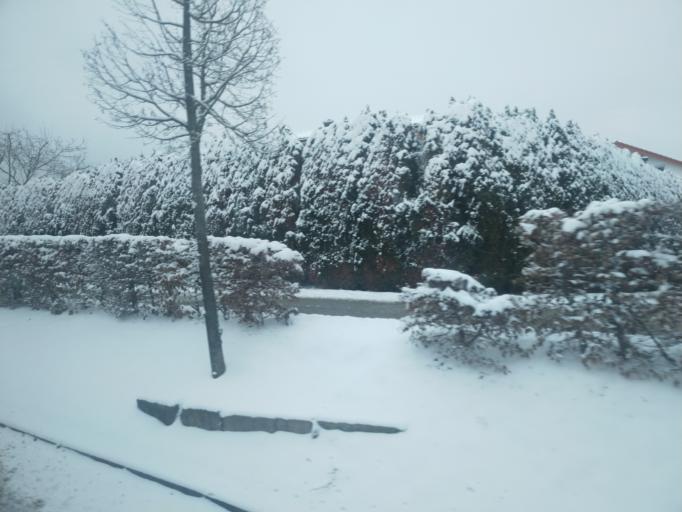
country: DE
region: Baden-Wuerttemberg
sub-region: Karlsruhe Region
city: Birkenfeld
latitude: 48.8738
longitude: 8.6334
